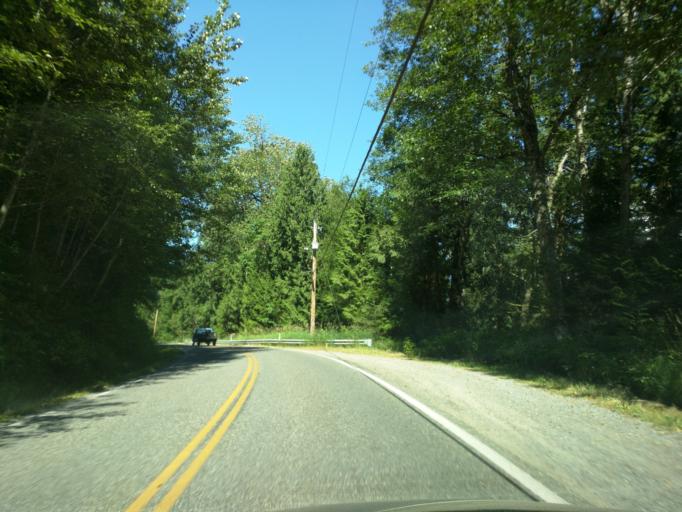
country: US
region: Washington
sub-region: Whatcom County
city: Sumas
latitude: 48.9417
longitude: -122.2398
